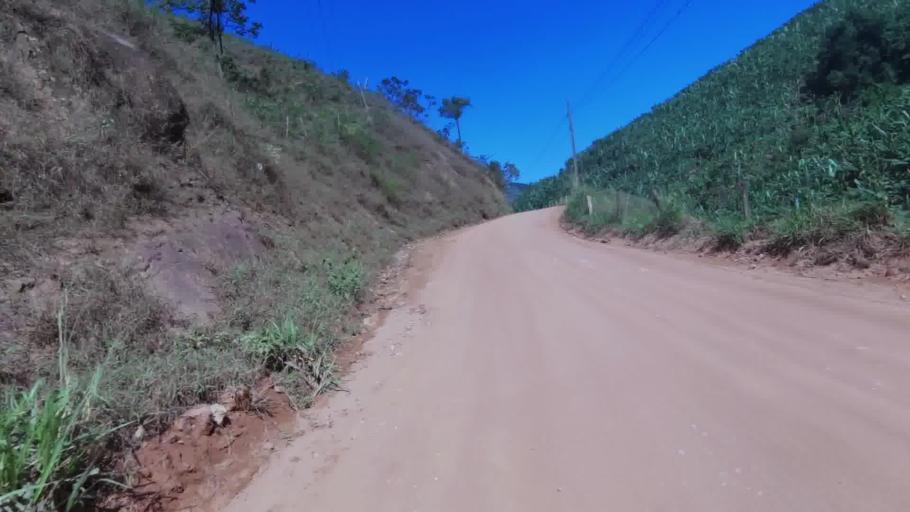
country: BR
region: Espirito Santo
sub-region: Alfredo Chaves
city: Alfredo Chaves
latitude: -20.6474
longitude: -40.8015
